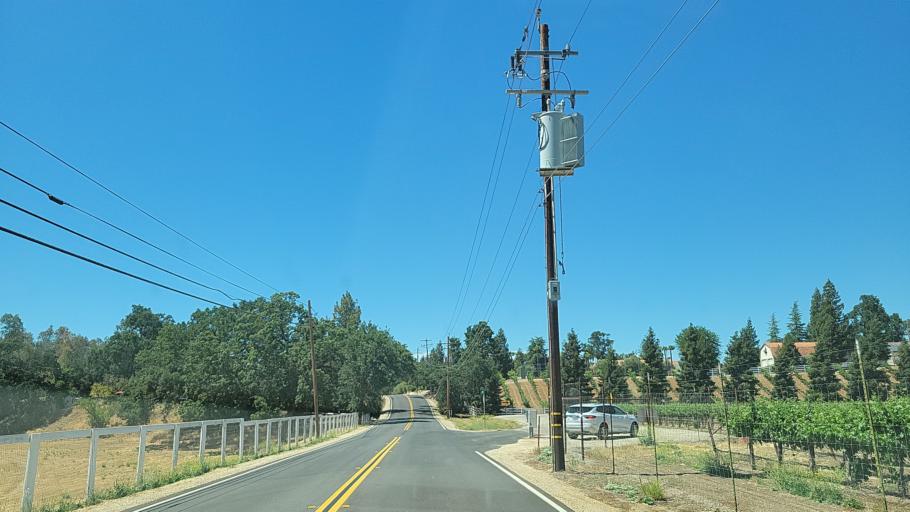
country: US
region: California
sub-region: San Luis Obispo County
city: Atascadero
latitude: 35.4989
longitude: -120.6476
